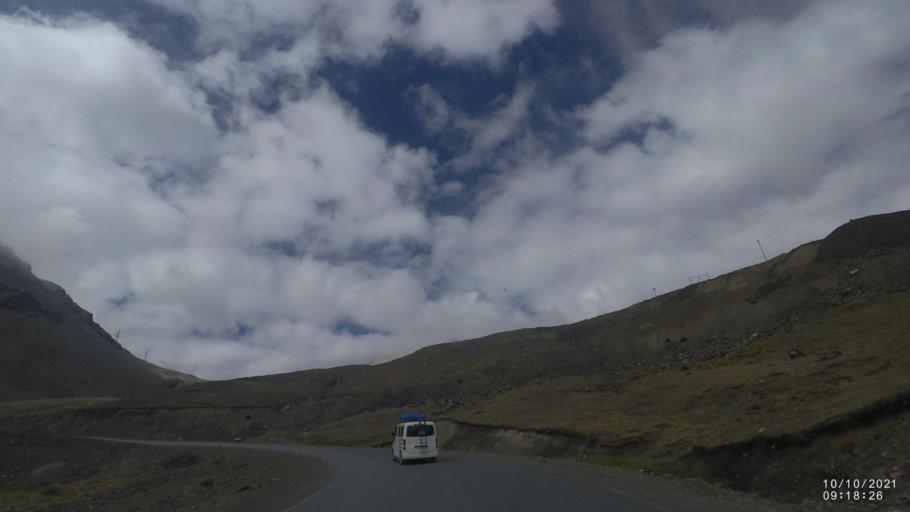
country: BO
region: La Paz
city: Quime
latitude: -17.0530
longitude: -67.2984
